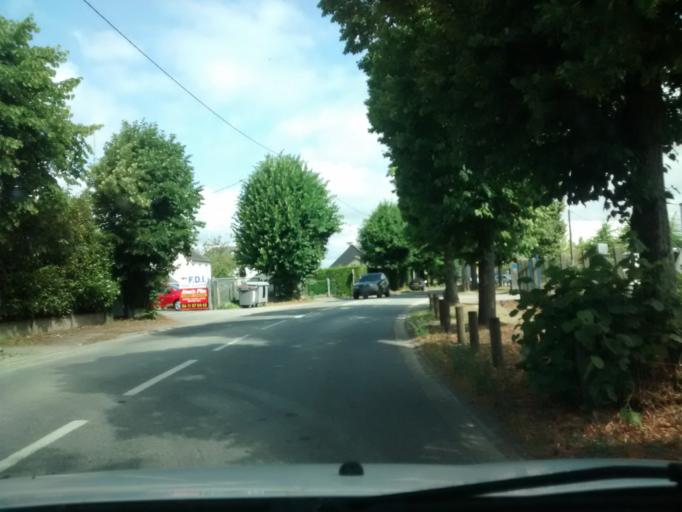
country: FR
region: Brittany
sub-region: Departement d'Ille-et-Vilaine
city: Chantepie
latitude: 48.1029
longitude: -1.6319
